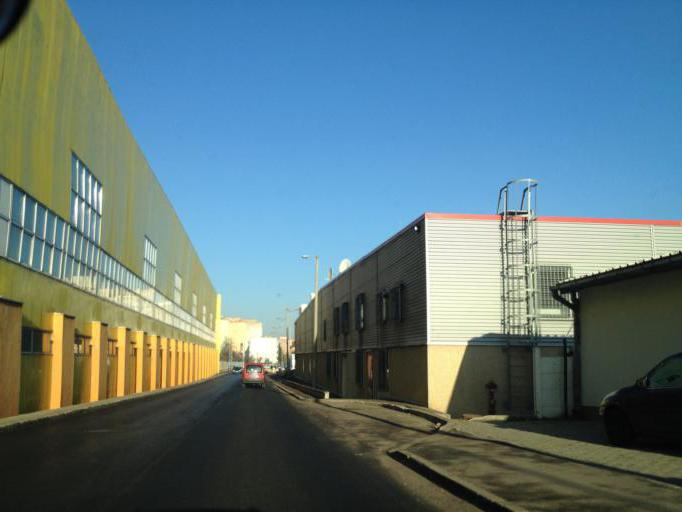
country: RO
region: Brasov
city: Brasov
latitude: 45.6317
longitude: 25.6349
